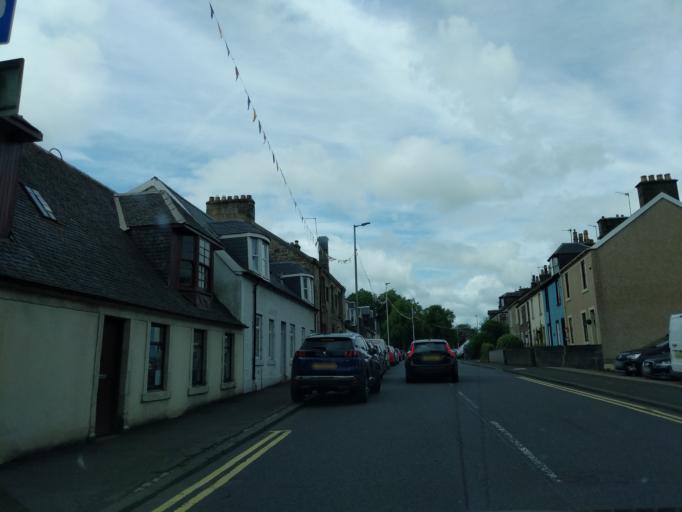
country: GB
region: Scotland
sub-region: South Lanarkshire
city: Strathaven
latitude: 55.6803
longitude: -4.0677
